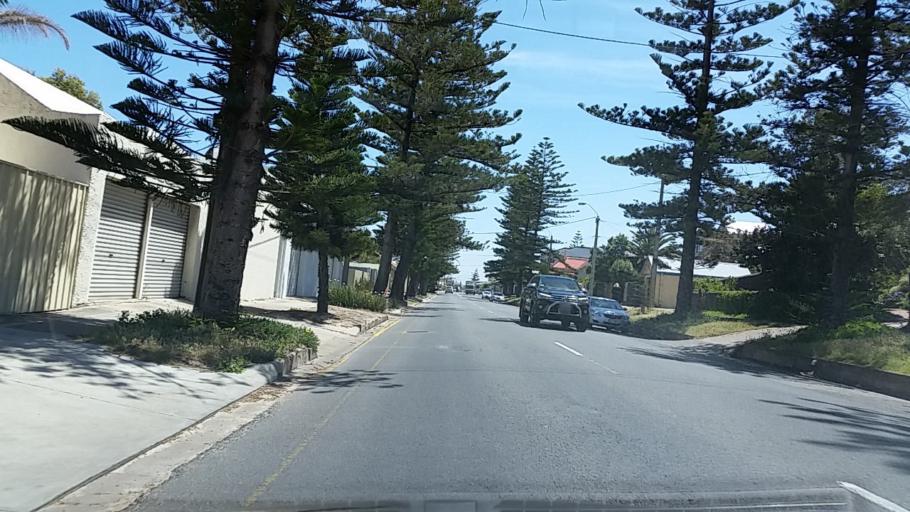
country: AU
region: South Australia
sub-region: Charles Sturt
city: Henley Beach
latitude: -34.9274
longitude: 138.4966
